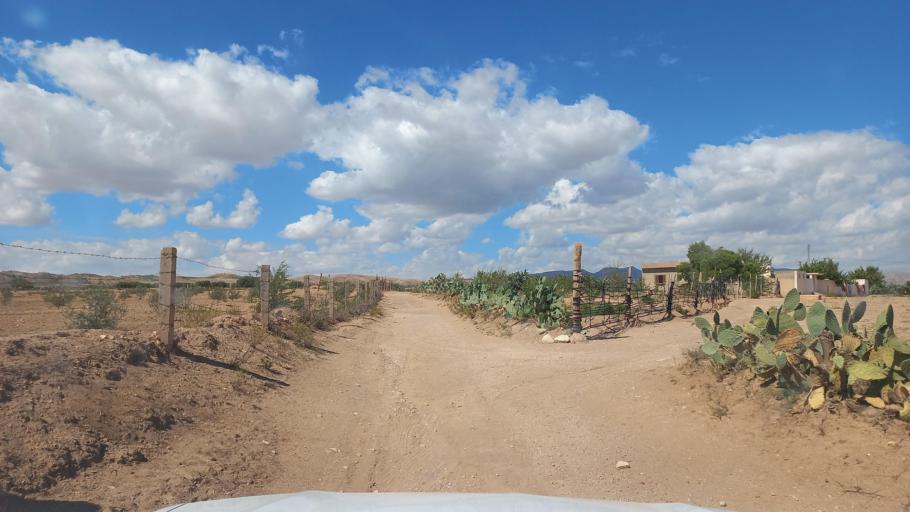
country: TN
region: Al Qasrayn
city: Sbiba
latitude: 35.3535
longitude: 9.0193
